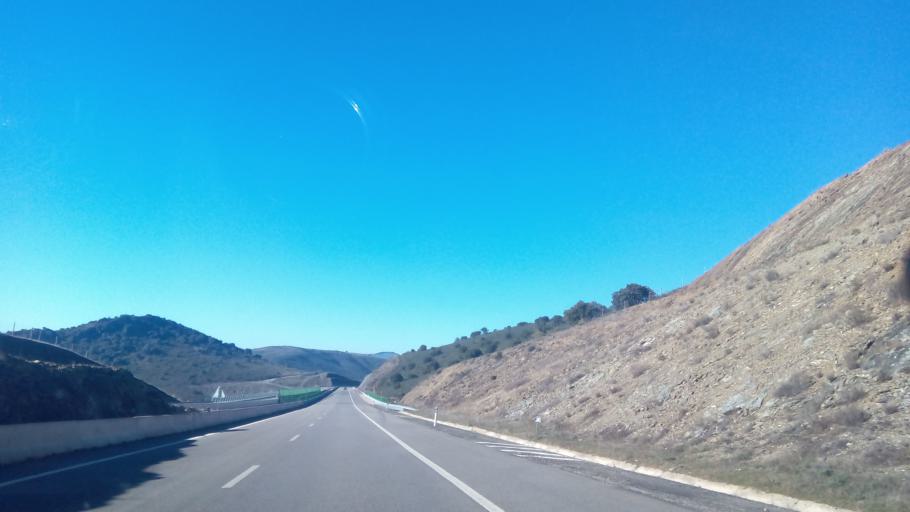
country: PT
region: Braganca
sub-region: Braganca Municipality
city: Braganca
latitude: 41.7695
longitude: -6.6627
